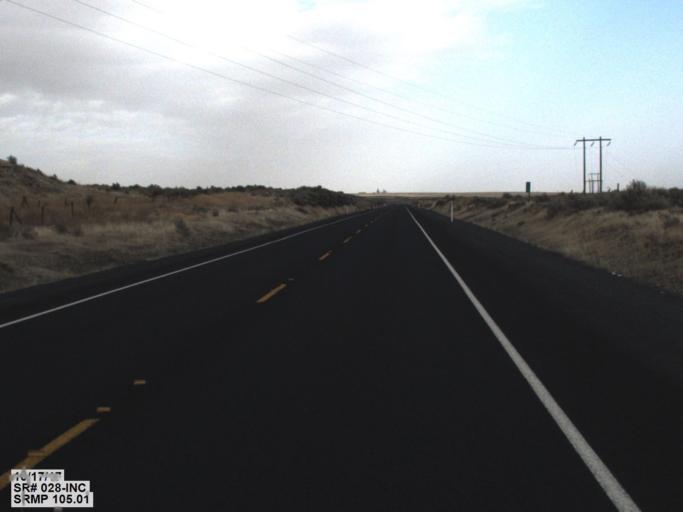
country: US
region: Washington
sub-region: Adams County
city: Ritzville
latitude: 47.3652
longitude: -118.4650
